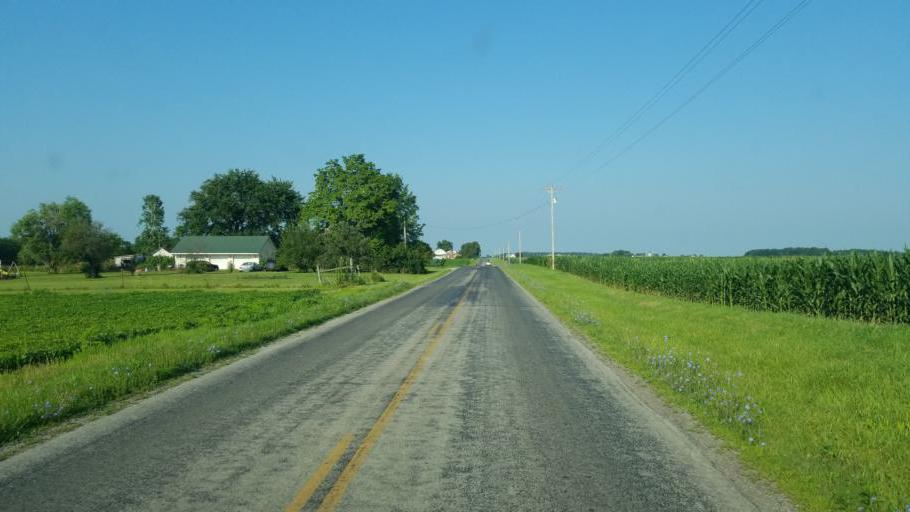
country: US
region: Ohio
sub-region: Union County
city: Richwood
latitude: 40.5453
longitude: -83.4438
